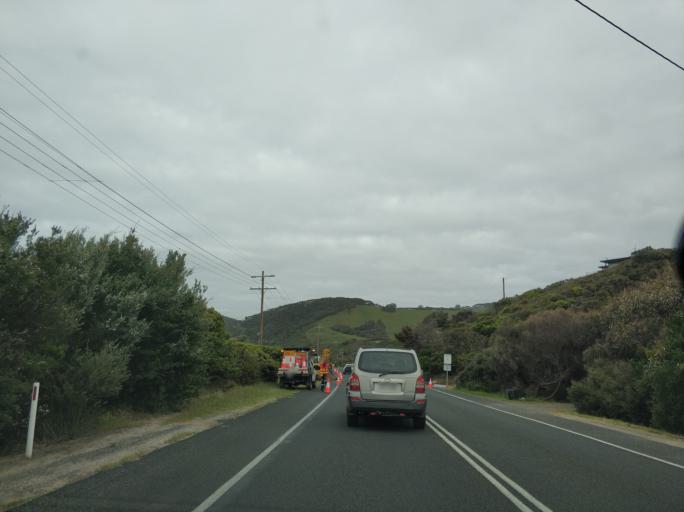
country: AU
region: Victoria
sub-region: Surf Coast
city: Anglesea
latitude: -38.4724
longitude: 144.0431
